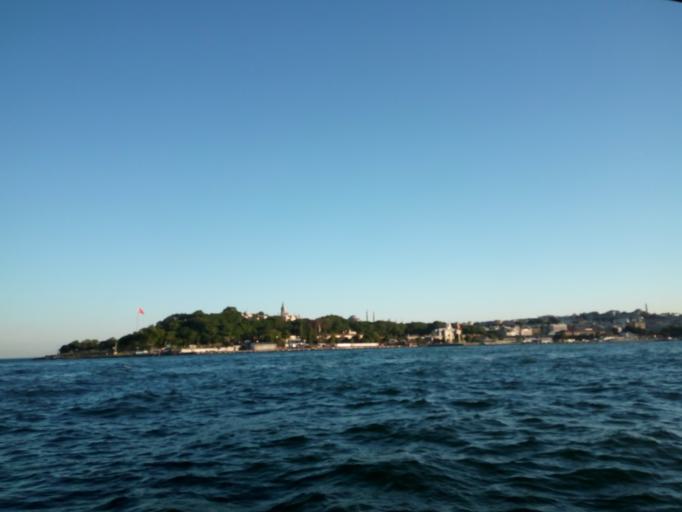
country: TR
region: Istanbul
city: Eminoenue
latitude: 41.0218
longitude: 28.9854
